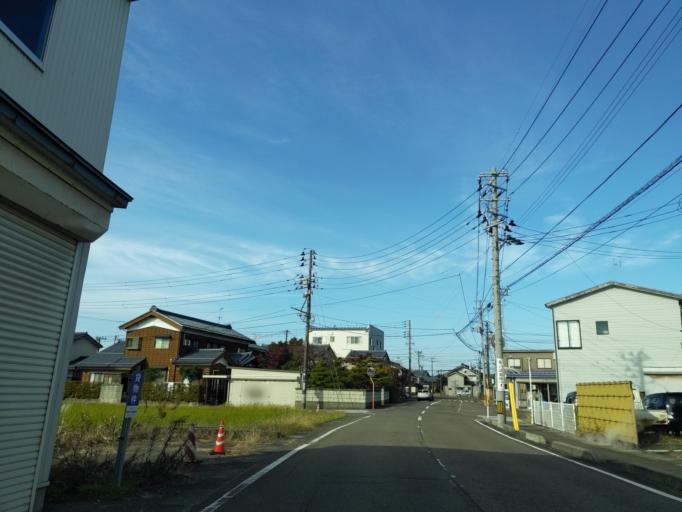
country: JP
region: Niigata
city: Sanjo
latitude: 37.6163
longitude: 138.9437
